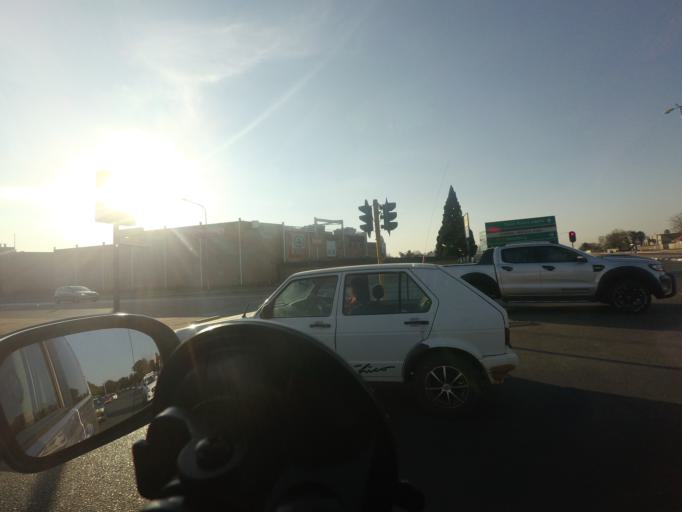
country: ZA
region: Gauteng
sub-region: Sedibeng District Municipality
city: Vereeniging
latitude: -26.6577
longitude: 27.9614
